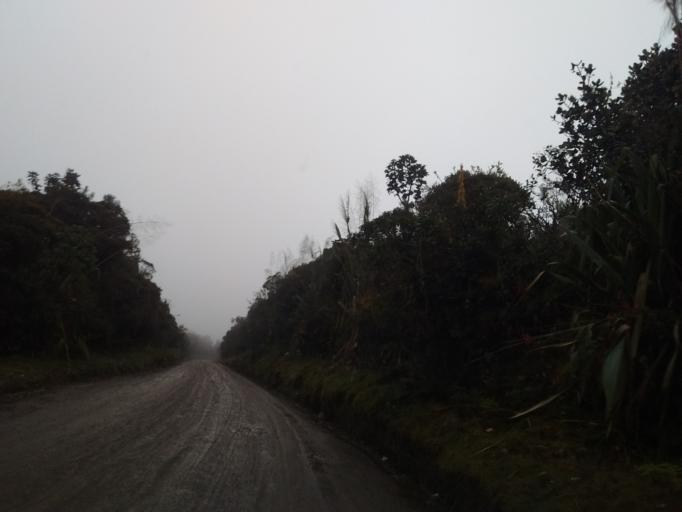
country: CO
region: Cauca
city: Paispamba
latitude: 2.1479
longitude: -76.4426
